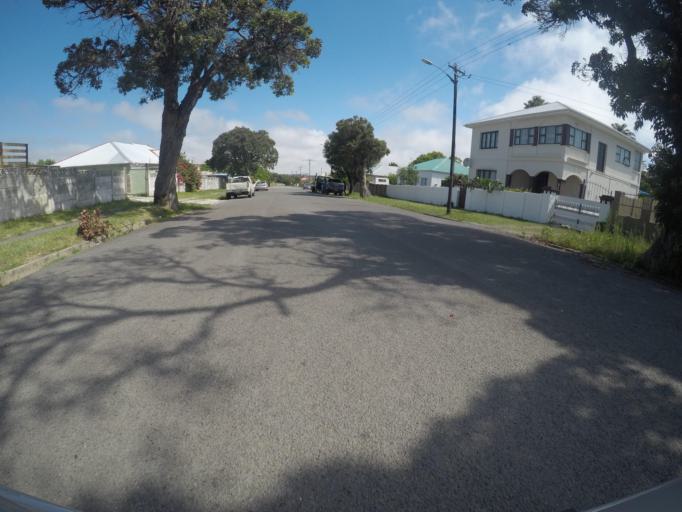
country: ZA
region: Eastern Cape
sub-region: Buffalo City Metropolitan Municipality
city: East London
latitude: -32.9754
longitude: 27.8970
